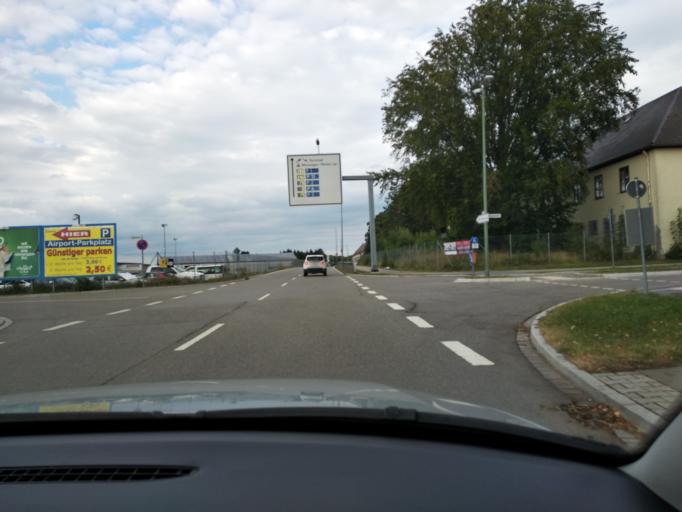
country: DE
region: Bavaria
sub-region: Swabia
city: Memmingerberg
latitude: 47.9907
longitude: 10.2204
